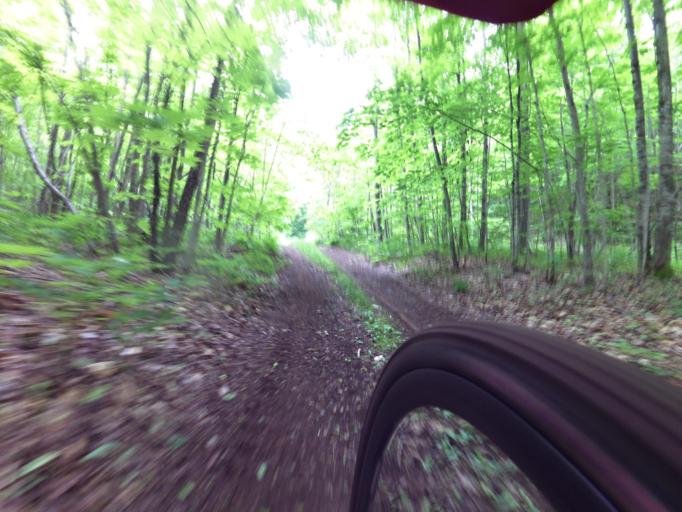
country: CA
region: Ontario
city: Arnprior
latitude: 45.1833
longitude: -76.5321
